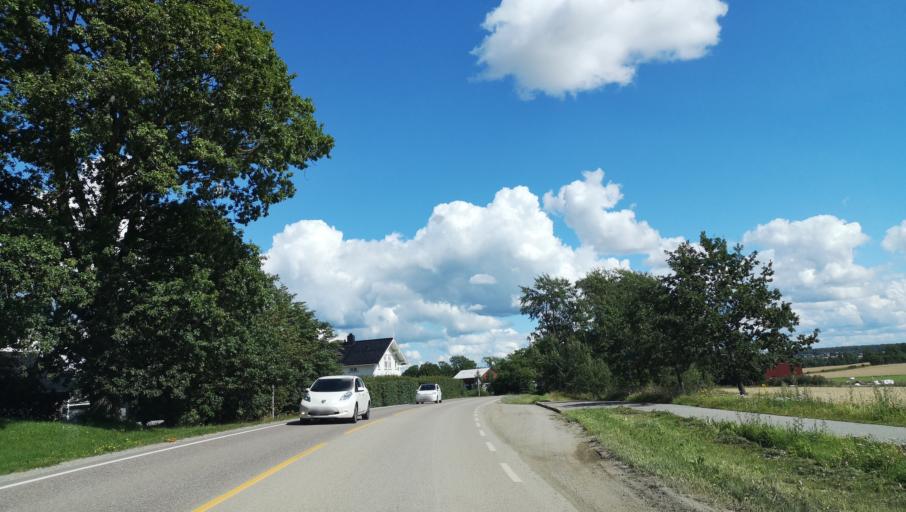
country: NO
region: Akershus
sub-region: Vestby
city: Vestby
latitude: 59.6593
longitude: 10.7260
